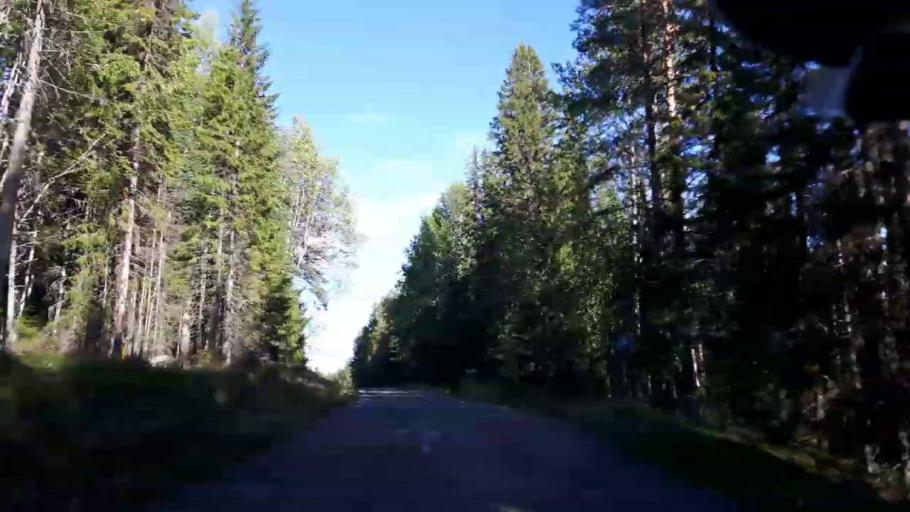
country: SE
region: Jaemtland
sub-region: Ragunda Kommun
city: Hammarstrand
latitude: 63.5281
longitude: 16.0732
